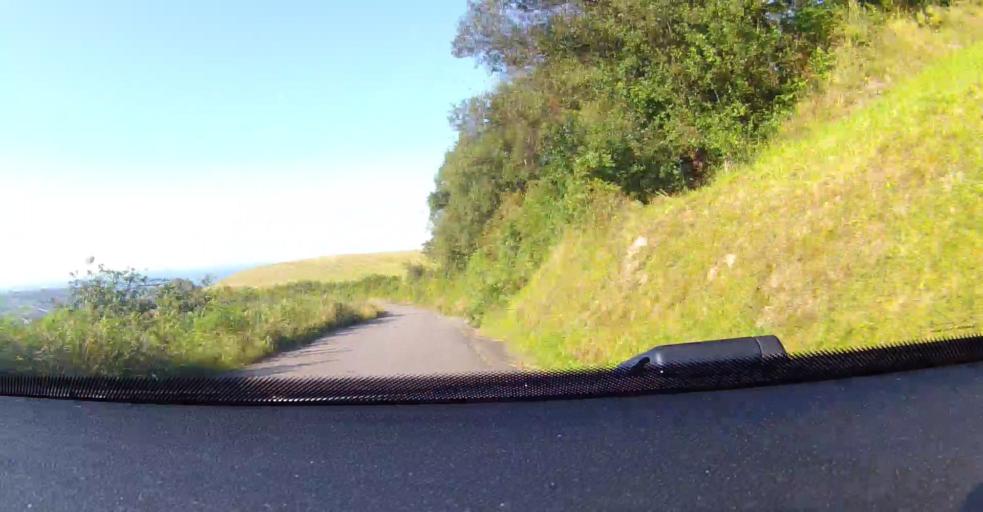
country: ES
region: Asturias
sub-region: Province of Asturias
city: Villaviciosa
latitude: 43.4880
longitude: -5.3917
